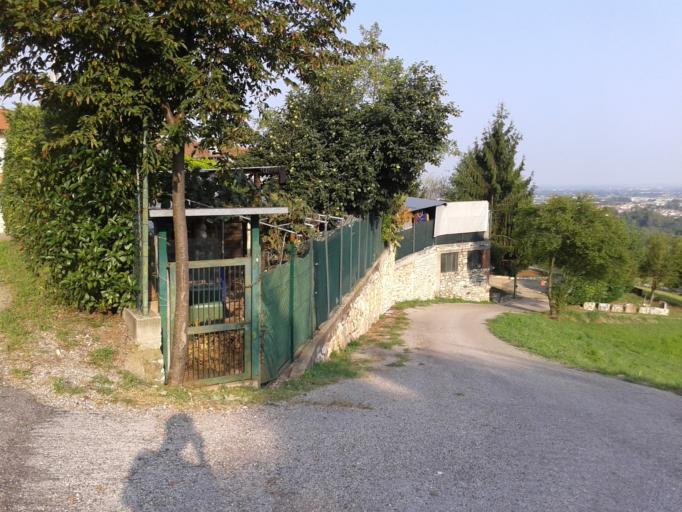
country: IT
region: Veneto
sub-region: Provincia di Vicenza
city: Monte di Malo
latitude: 45.6712
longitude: 11.3715
